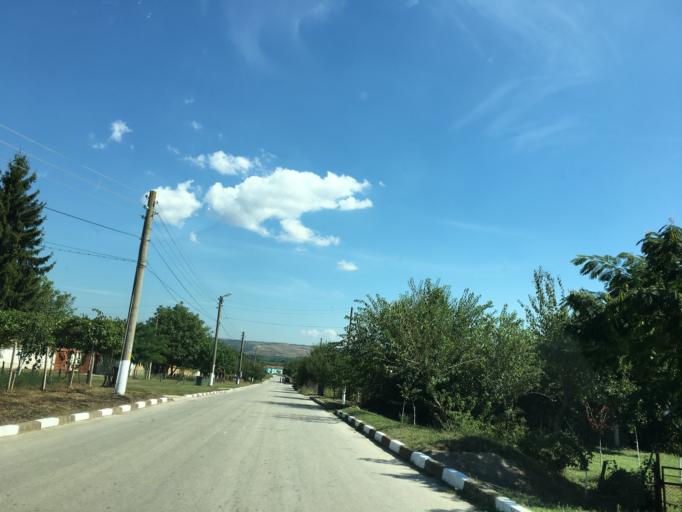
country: RO
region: Olt
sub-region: Comuna Orlea
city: Orlea
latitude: 43.6383
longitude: 24.3918
